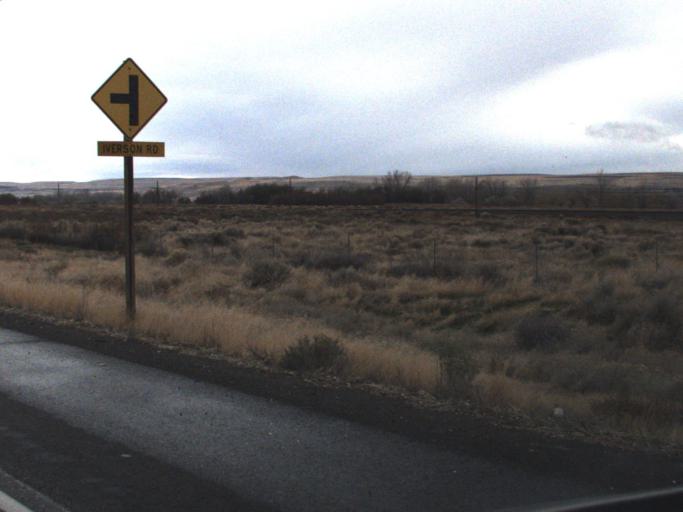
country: US
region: Washington
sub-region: Walla Walla County
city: Burbank
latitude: 46.1477
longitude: -118.9386
